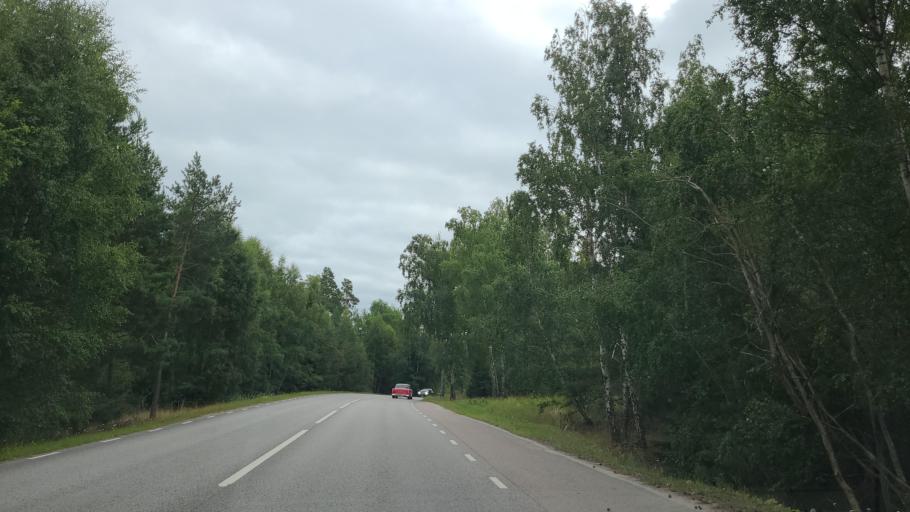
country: SE
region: Uppsala
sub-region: Habo Kommun
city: Balsta
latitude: 59.5415
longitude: 17.5636
